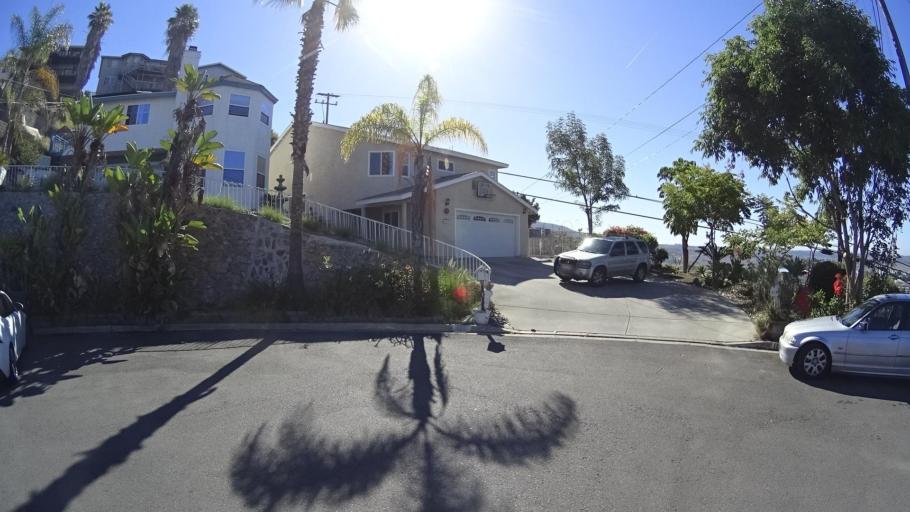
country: US
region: California
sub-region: San Diego County
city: La Presa
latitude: 32.7151
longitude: -116.9884
